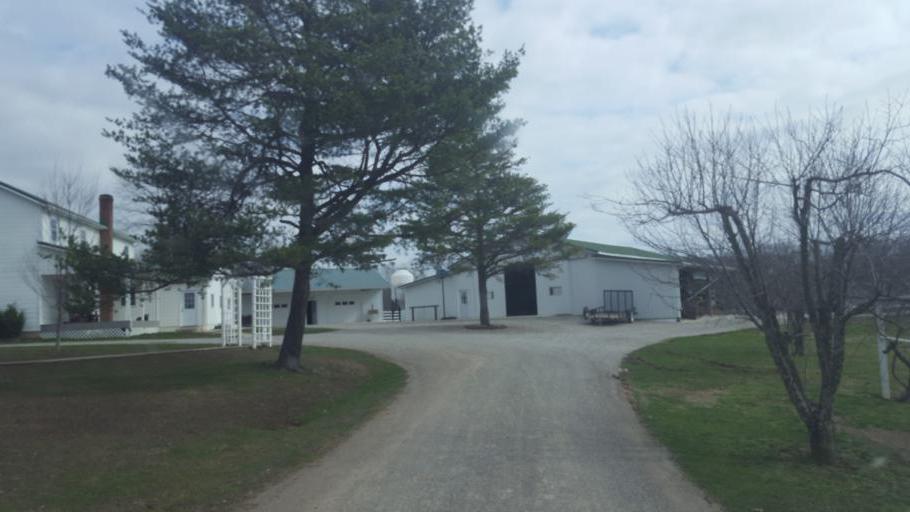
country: US
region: Ohio
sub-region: Gallia County
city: Gallipolis
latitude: 38.7202
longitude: -82.3535
